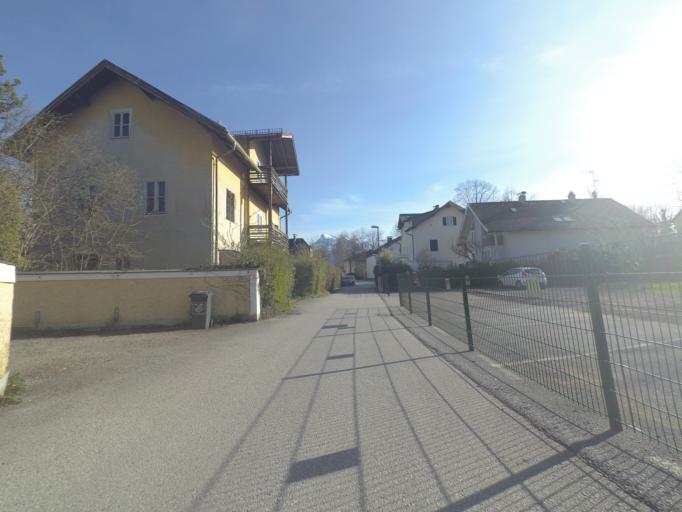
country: AT
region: Salzburg
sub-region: Salzburg Stadt
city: Salzburg
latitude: 47.8028
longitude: 13.0219
